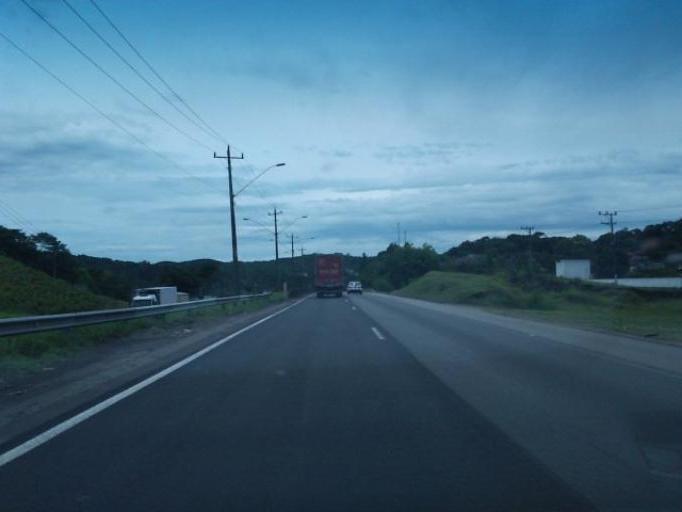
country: BR
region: Sao Paulo
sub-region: Sao Lourenco Da Serra
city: Sao Lourenco da Serra
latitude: -23.9158
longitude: -46.9893
